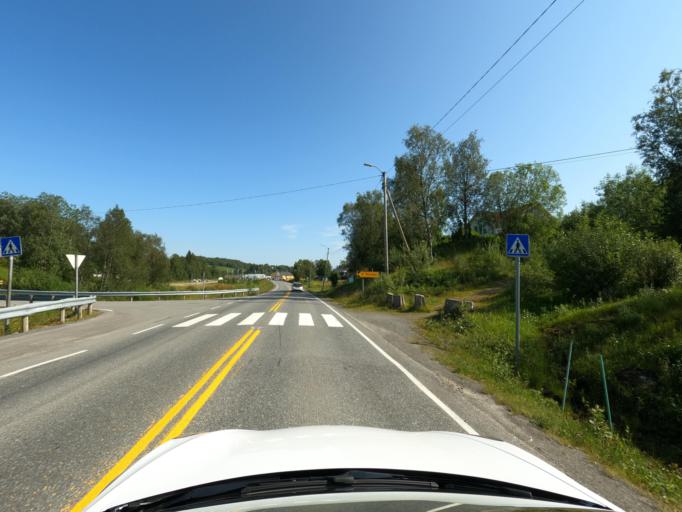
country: NO
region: Nordland
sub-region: Ballangen
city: Ballangen
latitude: 68.3417
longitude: 16.8215
